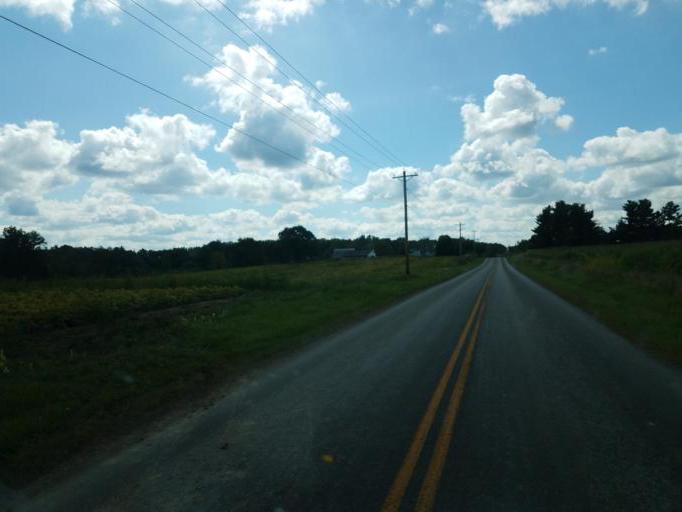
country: US
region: Ohio
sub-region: Wayne County
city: West Salem
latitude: 41.0155
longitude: -82.1265
